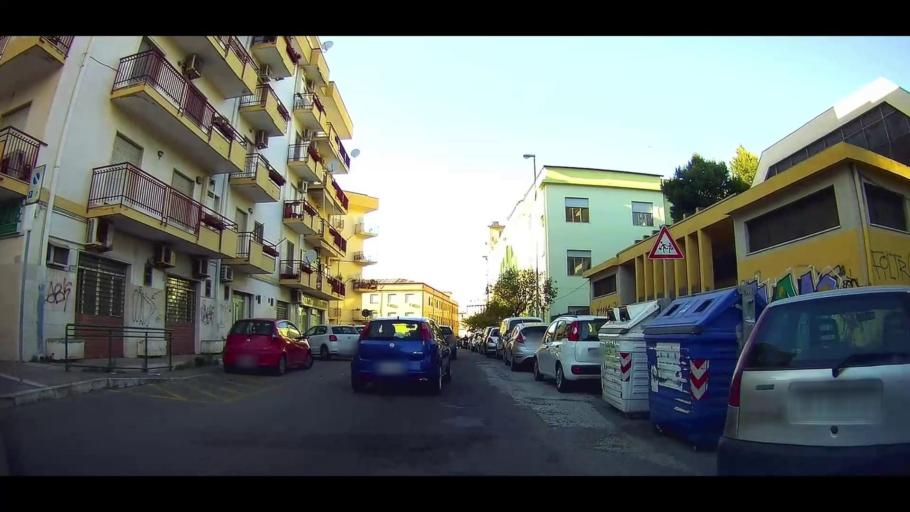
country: IT
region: Calabria
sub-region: Provincia di Crotone
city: Crotone
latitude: 39.0766
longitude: 17.1281
